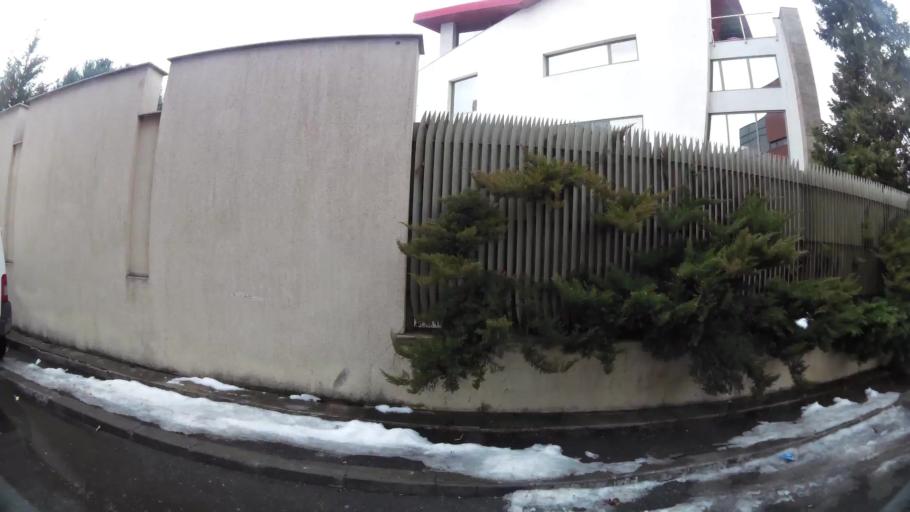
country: RO
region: Bucuresti
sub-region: Municipiul Bucuresti
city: Bucharest
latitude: 44.4823
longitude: 26.0878
